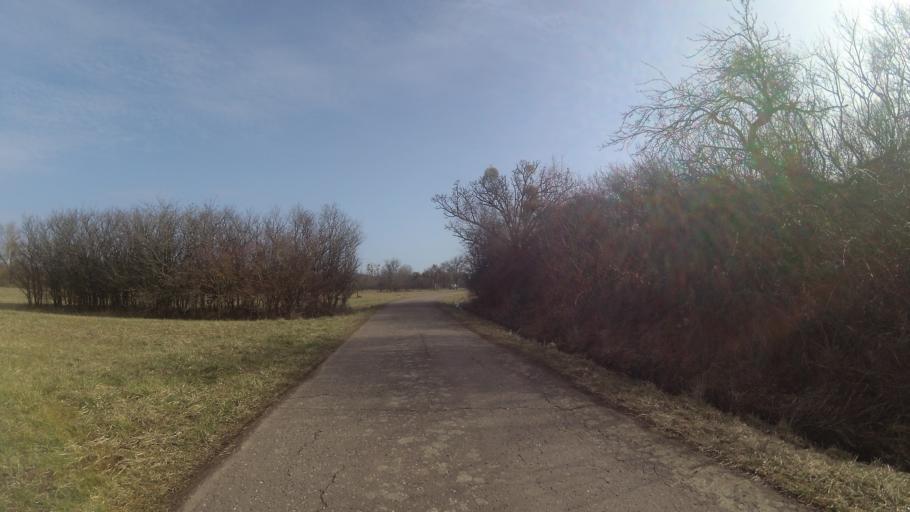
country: DE
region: Saarland
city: Rehlingen-Siersburg
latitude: 49.3277
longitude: 6.6587
